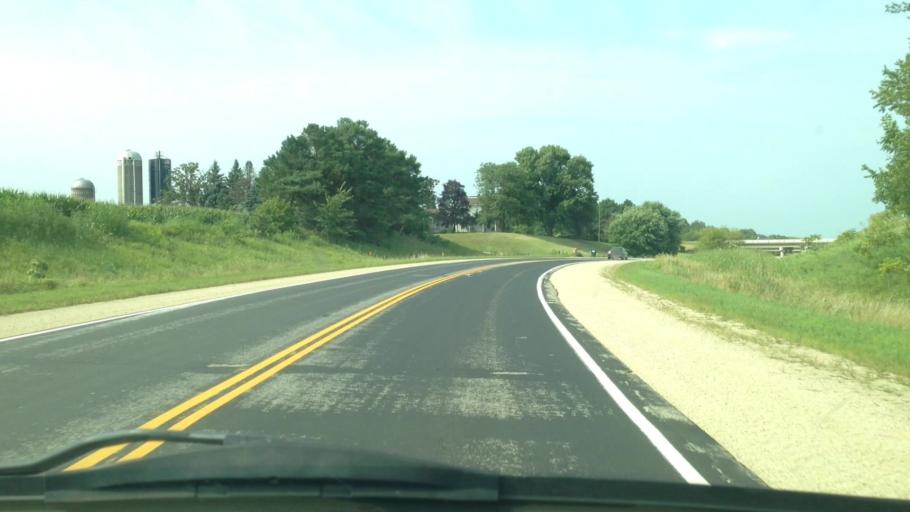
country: US
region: Minnesota
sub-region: Winona County
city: Lewiston
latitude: 43.9305
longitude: -91.9599
